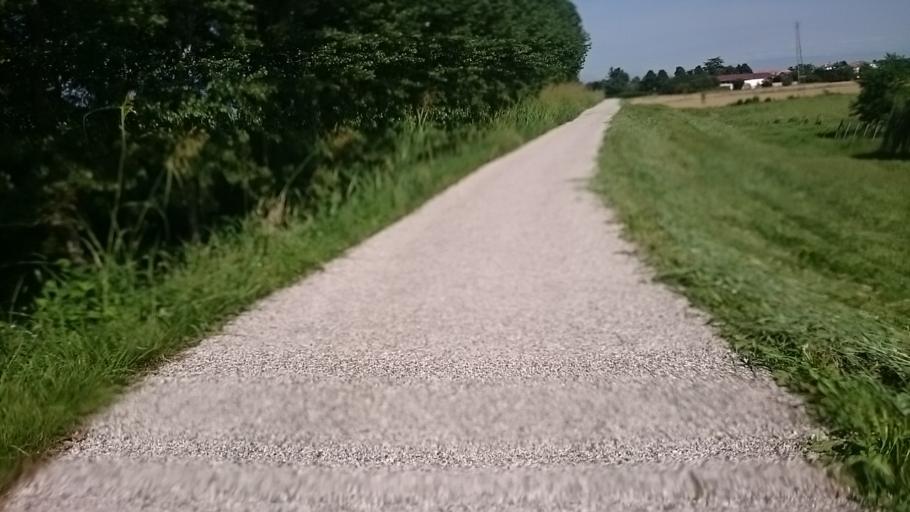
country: IT
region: Veneto
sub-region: Provincia di Padova
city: Saccolongo
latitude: 45.4071
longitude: 11.7529
